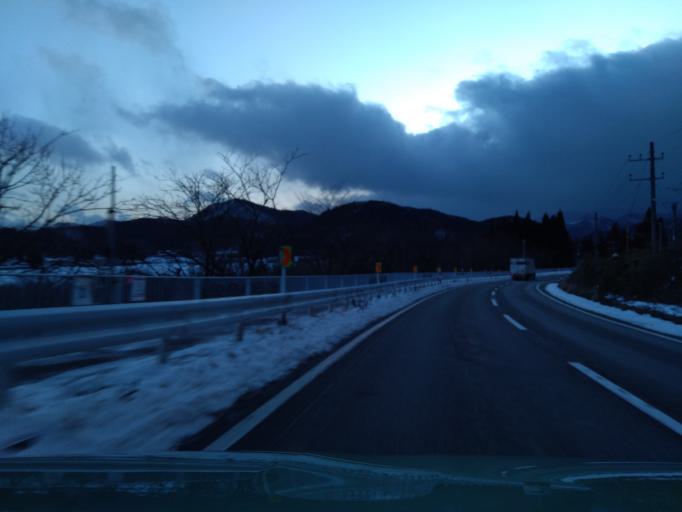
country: JP
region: Iwate
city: Shizukuishi
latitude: 39.6895
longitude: 140.9229
